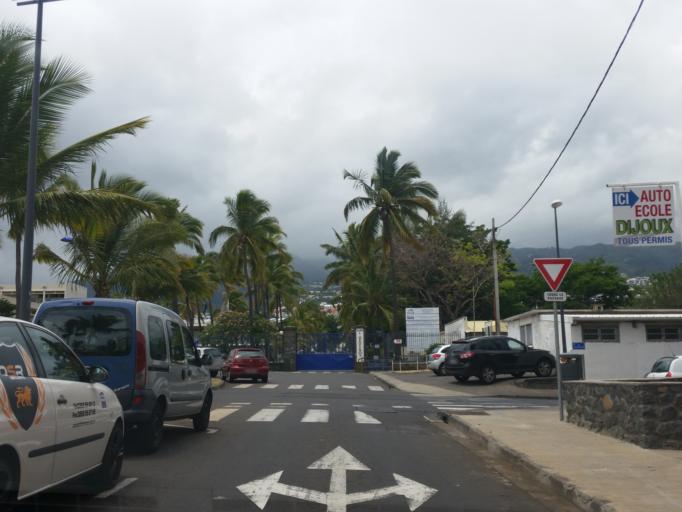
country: RE
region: Reunion
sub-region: Reunion
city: Saint-Denis
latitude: -20.8868
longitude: 55.4694
